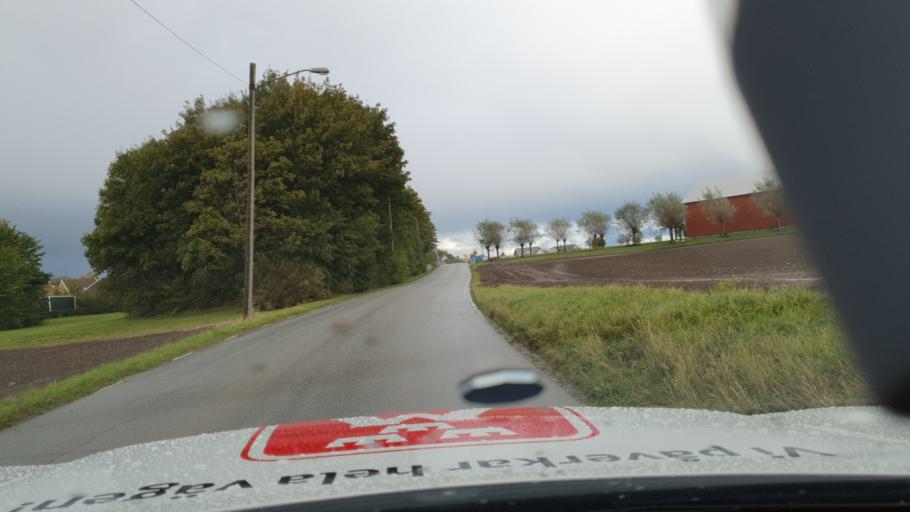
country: SE
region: Skane
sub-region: Malmo
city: Oxie
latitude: 55.5272
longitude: 13.0739
